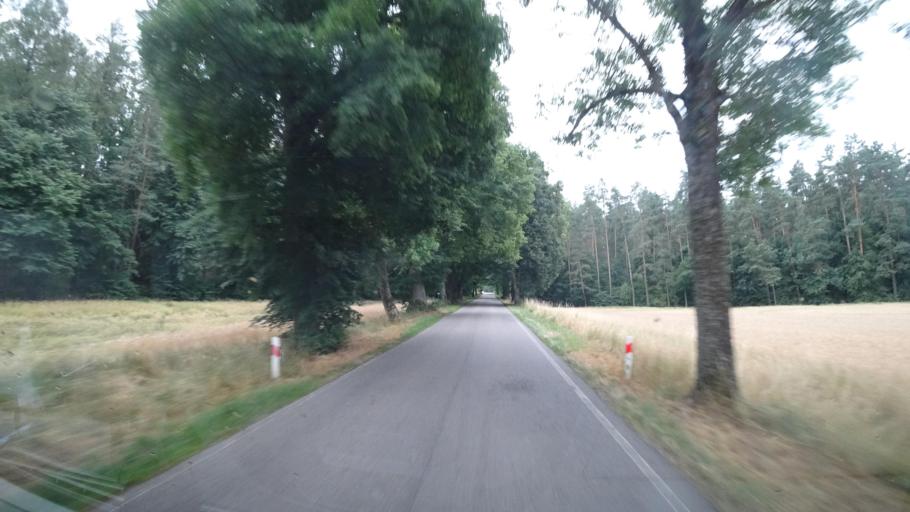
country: PL
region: Warmian-Masurian Voivodeship
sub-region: Powiat gizycki
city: Ryn
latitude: 53.8927
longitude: 21.5739
